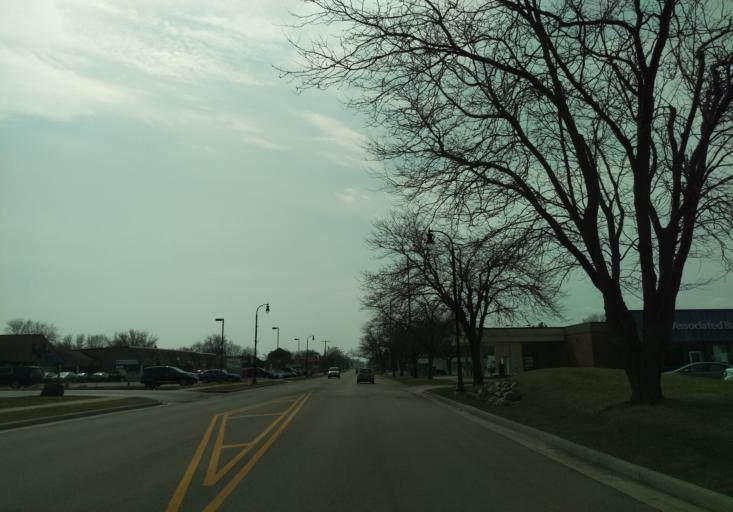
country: US
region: Wisconsin
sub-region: Dane County
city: Waunakee
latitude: 43.1908
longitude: -89.4618
